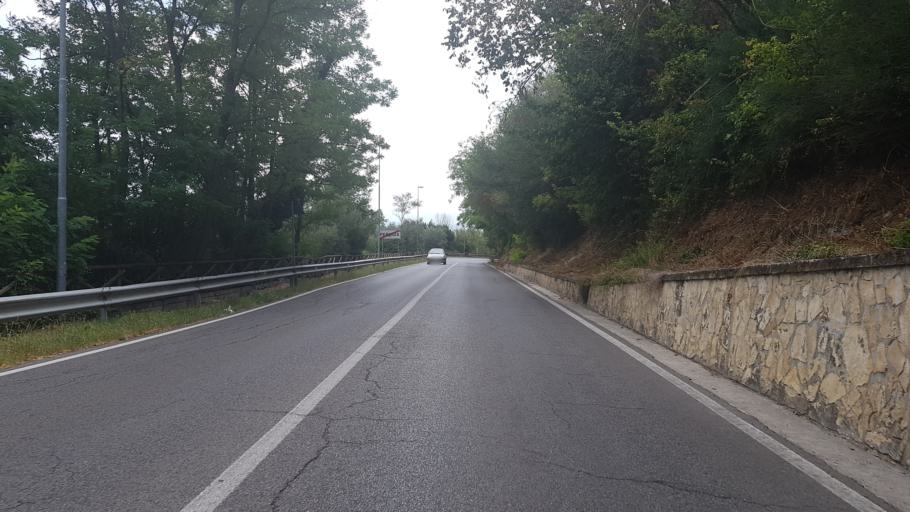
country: IT
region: Umbria
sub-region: Provincia di Perugia
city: San Martino in Campo
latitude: 43.0747
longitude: 12.4016
